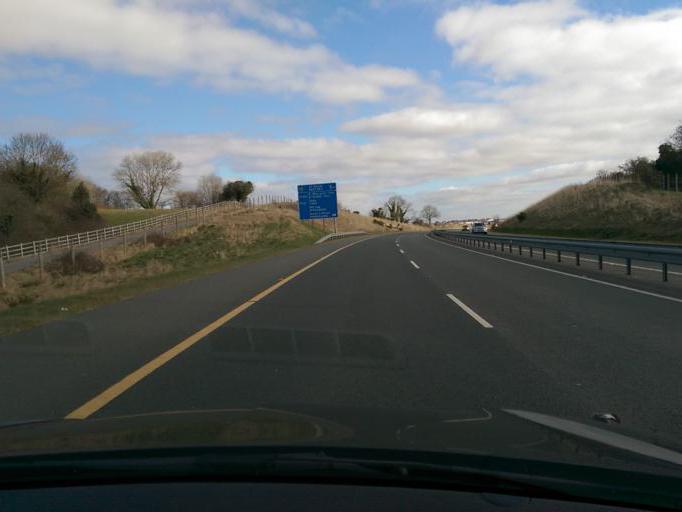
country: IE
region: Leinster
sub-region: An Iarmhi
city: Athlone
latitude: 53.4124
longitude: -8.0135
